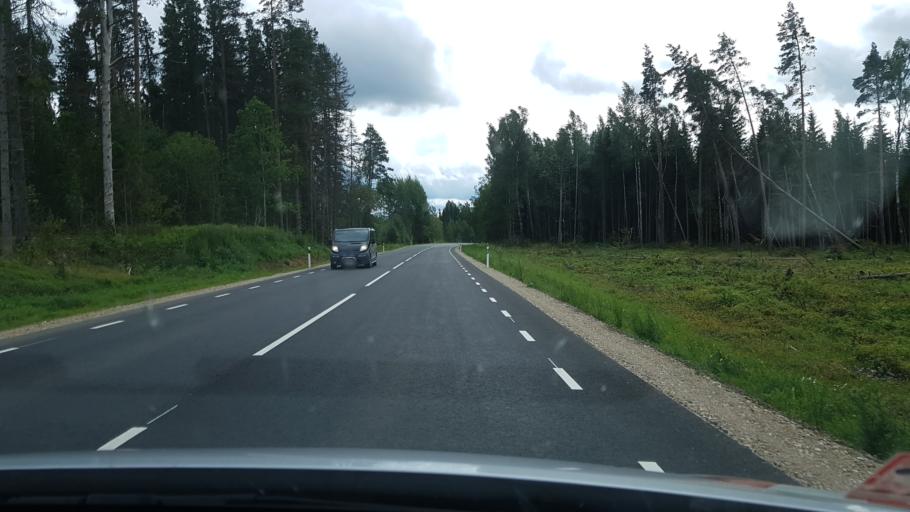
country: EE
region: Viljandimaa
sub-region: Karksi vald
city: Karksi-Nuia
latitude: 58.2201
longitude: 25.6172
